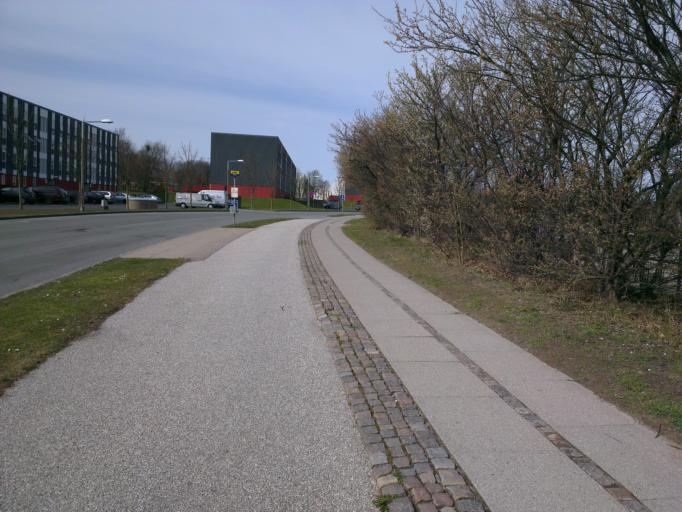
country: DK
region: Capital Region
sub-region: Frederikssund Kommune
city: Frederikssund
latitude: 55.8491
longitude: 12.0574
